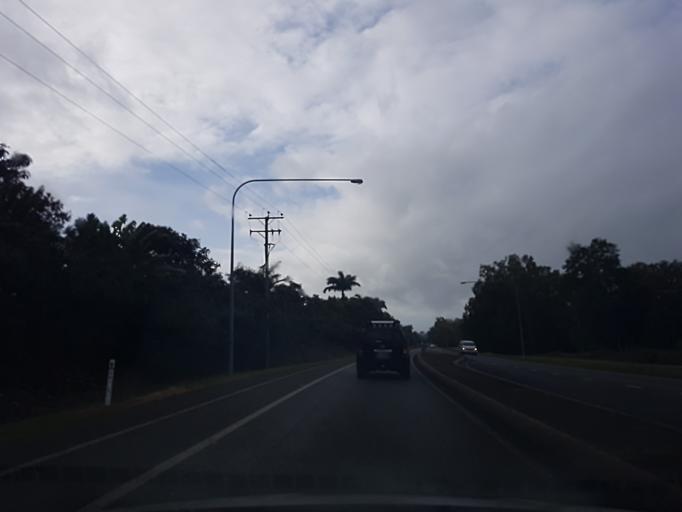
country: AU
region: Queensland
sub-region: Cairns
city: Trinity Beach
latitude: -16.7821
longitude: 145.6733
